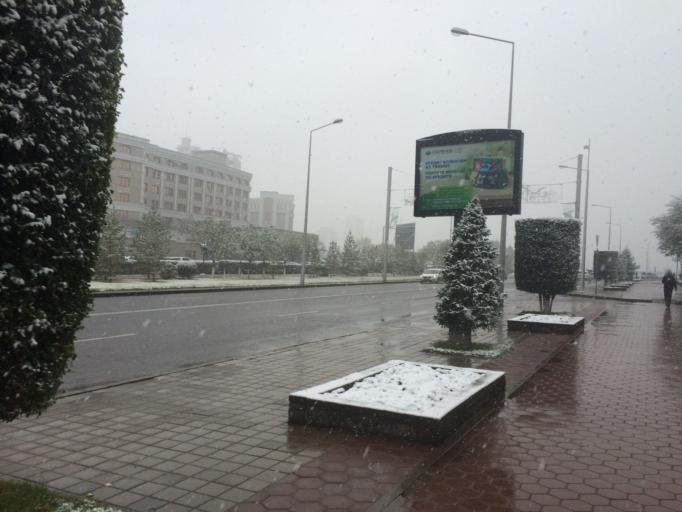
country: KZ
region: Astana Qalasy
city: Astana
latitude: 51.1333
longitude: 71.4166
